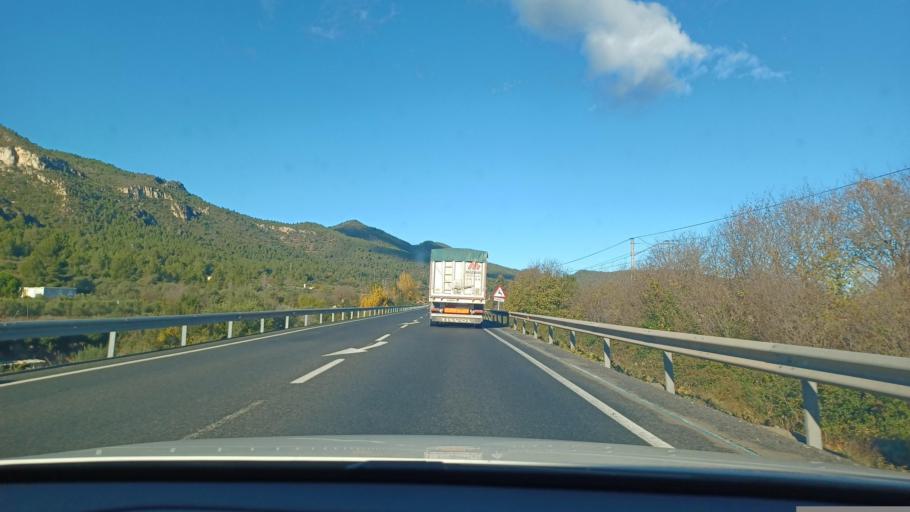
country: ES
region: Catalonia
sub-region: Provincia de Tarragona
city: Montblanc
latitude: 41.3236
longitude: 1.1810
